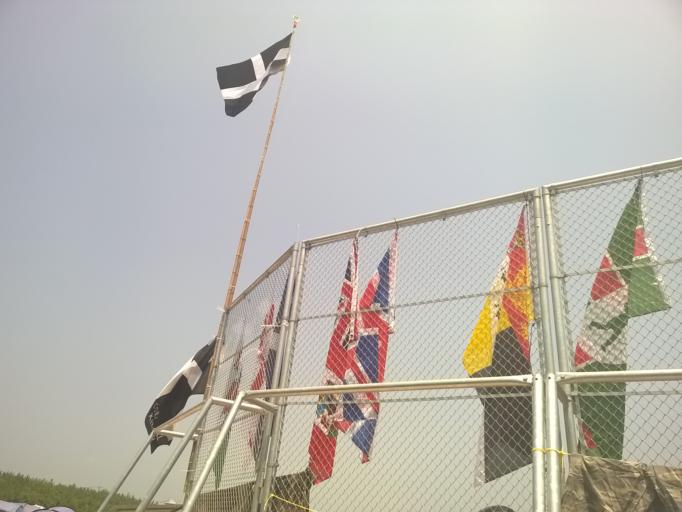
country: JP
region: Yamaguchi
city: Ogori-shimogo
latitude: 34.0036
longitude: 131.3661
